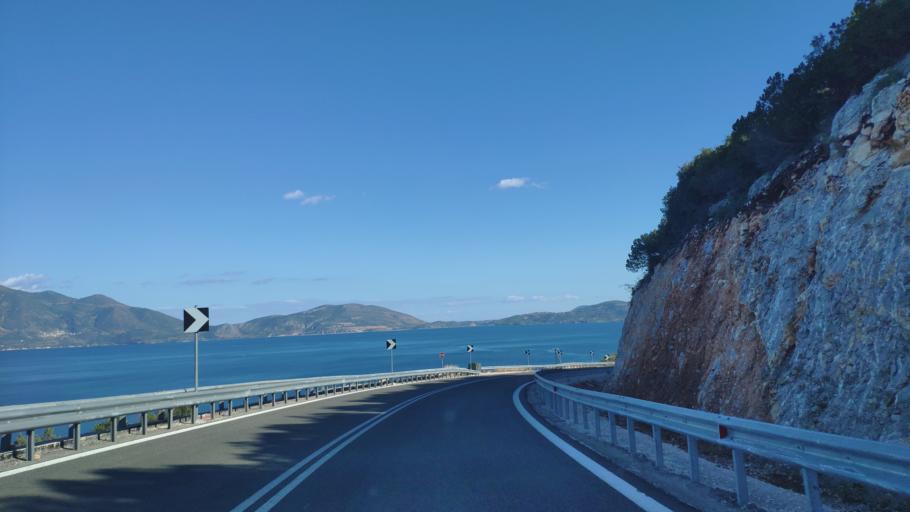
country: GR
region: Peloponnese
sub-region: Nomos Argolidos
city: Didyma
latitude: 37.5552
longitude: 23.2711
